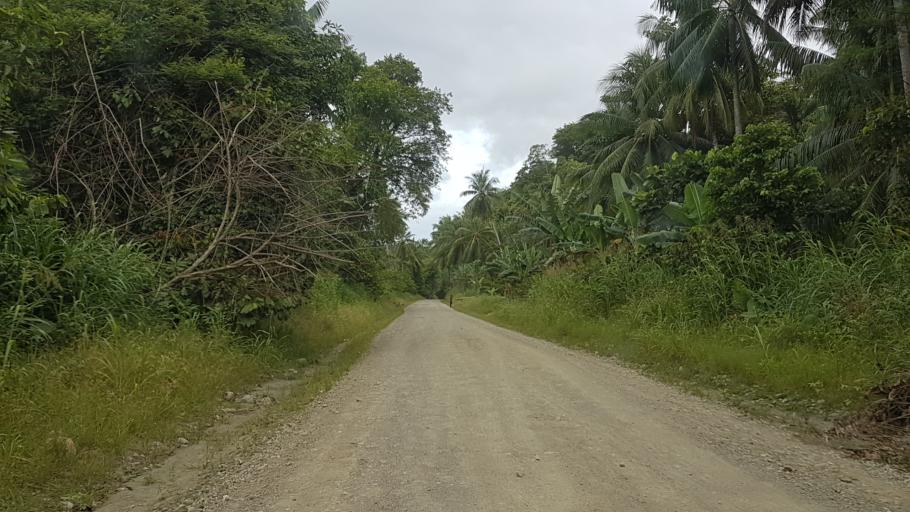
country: PG
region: East Sepik
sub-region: Wewak
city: Wewak
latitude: -3.4133
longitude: 143.3611
